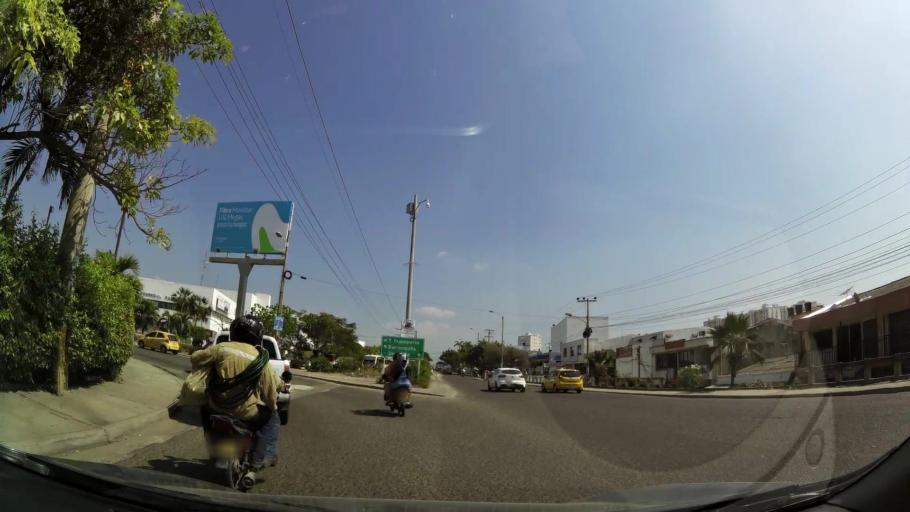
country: CO
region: Bolivar
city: Cartagena
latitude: 10.3921
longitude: -75.4813
